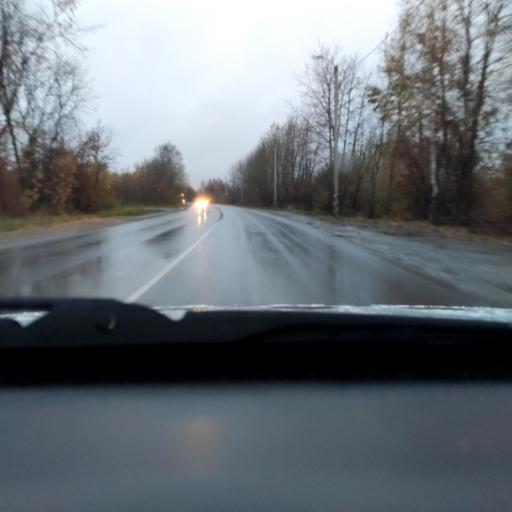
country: RU
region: Perm
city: Kondratovo
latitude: 57.9429
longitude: 56.1539
